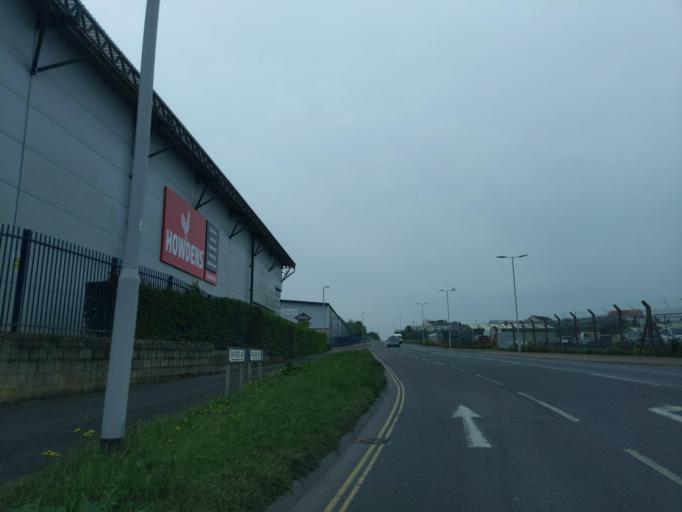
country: GB
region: England
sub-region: Plymouth
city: Plymouth
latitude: 50.3647
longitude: -4.1174
